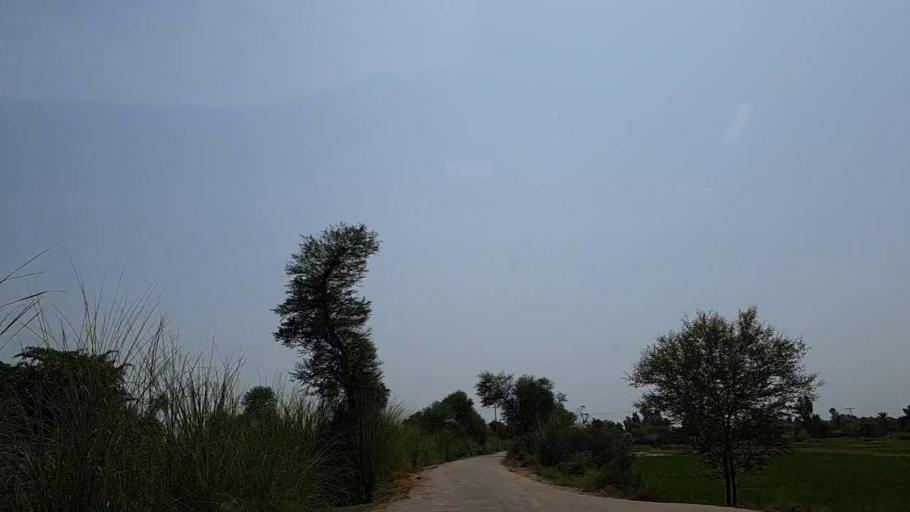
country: PK
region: Sindh
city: Adilpur
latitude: 27.9138
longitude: 69.3696
